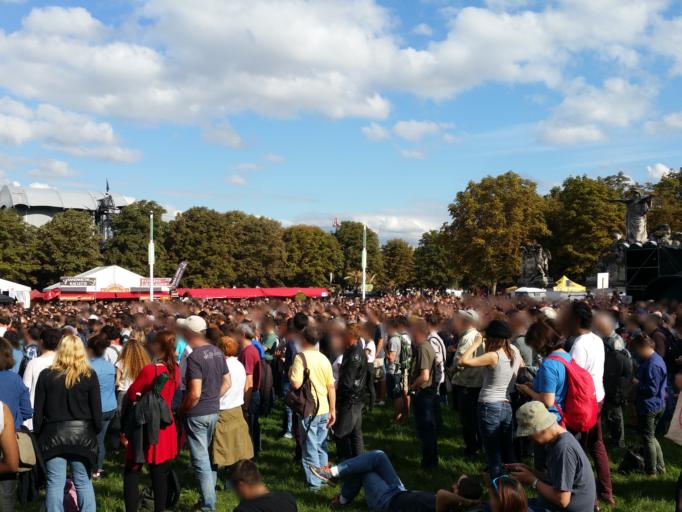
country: FR
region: Ile-de-France
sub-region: Departement des Hauts-de-Seine
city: Sevres
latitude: 48.8354
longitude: 2.2194
